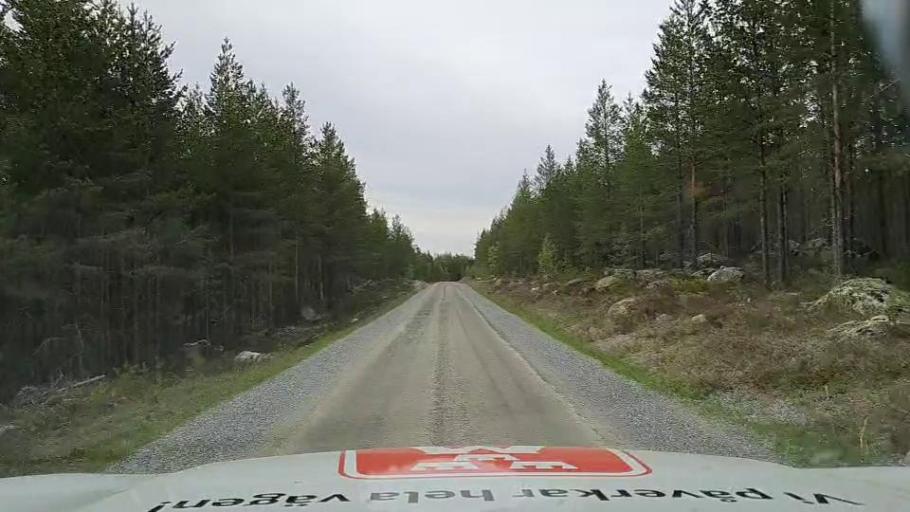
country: SE
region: Jaemtland
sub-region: Braecke Kommun
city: Braecke
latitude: 62.4677
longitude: 14.9175
